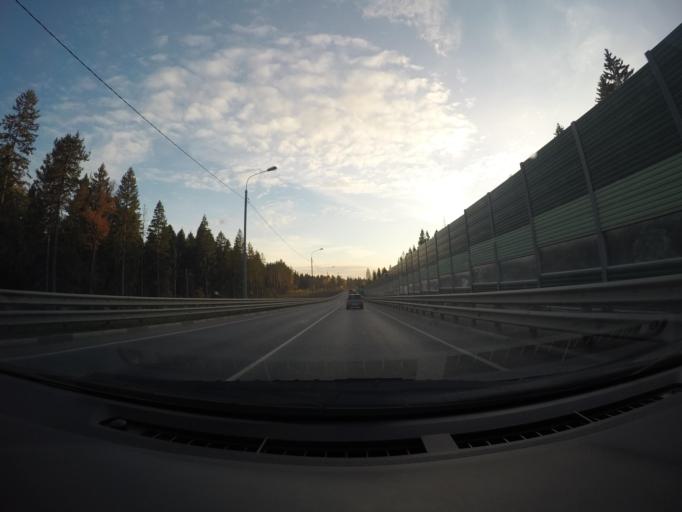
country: RU
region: Moskovskaya
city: Firsanovka
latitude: 55.9557
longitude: 37.2603
